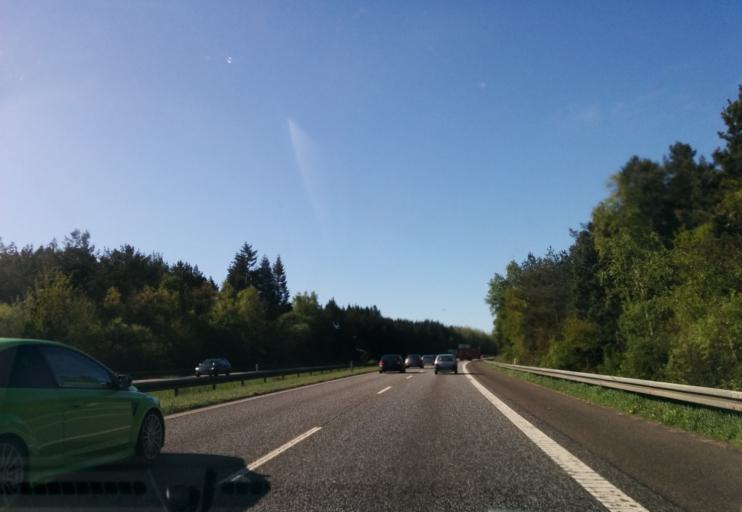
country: DK
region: Central Jutland
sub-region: Skanderborg Kommune
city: Skanderborg
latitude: 56.0132
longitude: 9.8818
